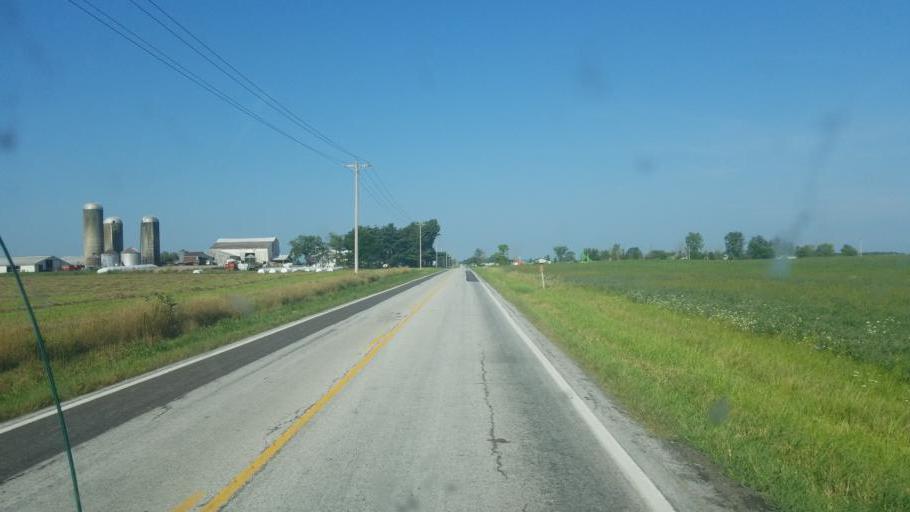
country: US
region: Ohio
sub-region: Lorain County
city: Wellington
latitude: 41.1003
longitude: -82.1381
